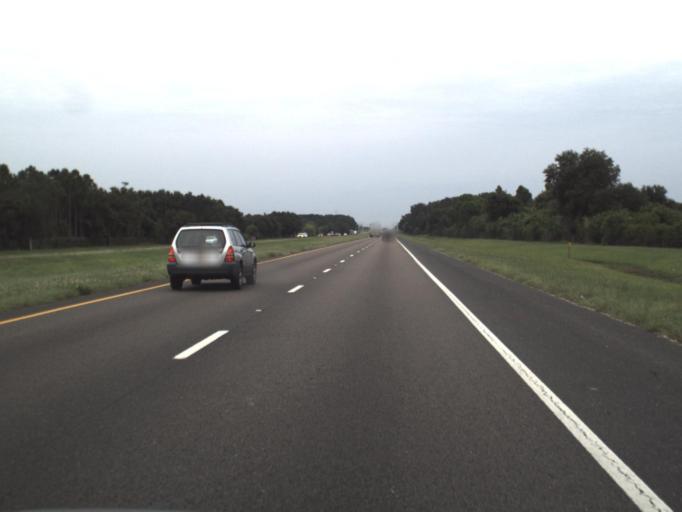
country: US
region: Florida
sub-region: Manatee County
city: Samoset
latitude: 27.4343
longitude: -82.5303
